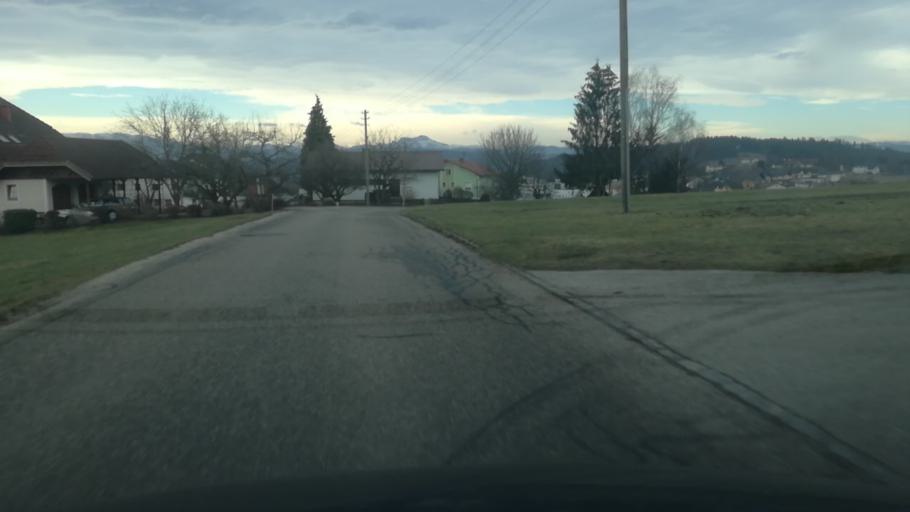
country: AT
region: Upper Austria
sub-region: Politischer Bezirk Vocklabruck
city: Neukirchen an der Vockla
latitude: 48.0475
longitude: 13.5395
